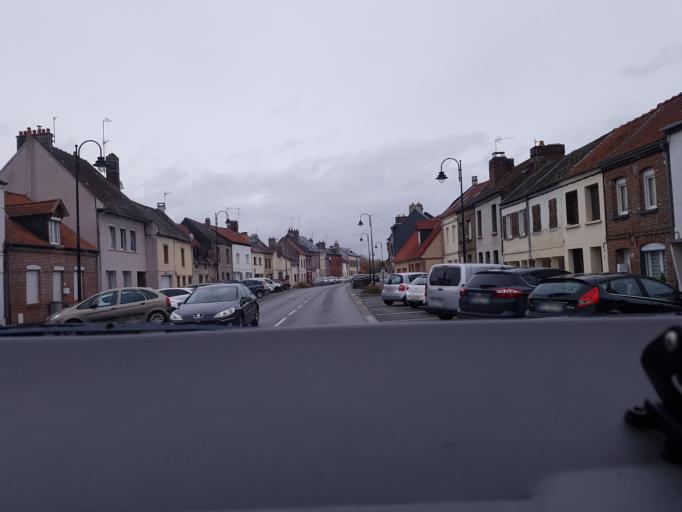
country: FR
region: Picardie
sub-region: Departement de la Somme
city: Abbeville
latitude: 50.1094
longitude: 1.8070
